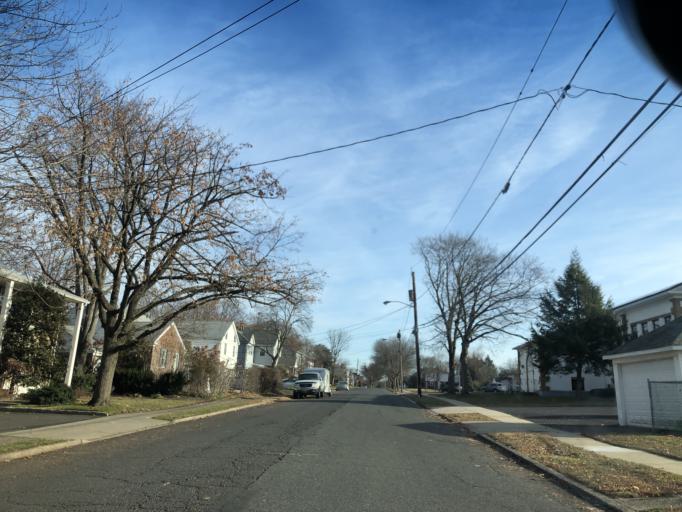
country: US
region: New Jersey
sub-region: Bergen County
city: Fair Lawn
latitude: 40.9281
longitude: -74.1302
